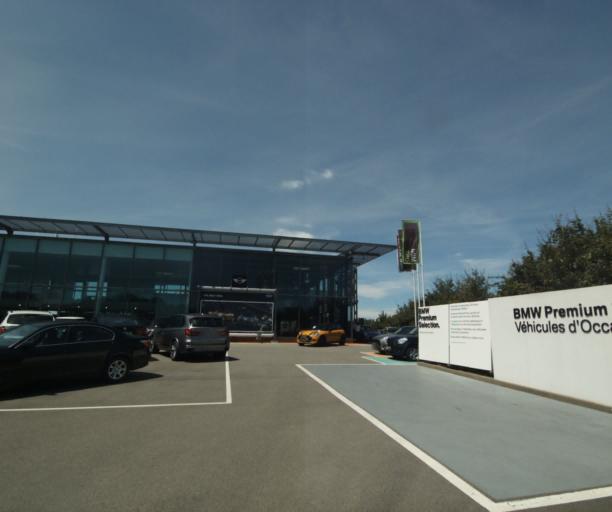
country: FR
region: Pays de la Loire
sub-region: Departement de la Mayenne
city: Change
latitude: 48.0843
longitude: -0.7913
